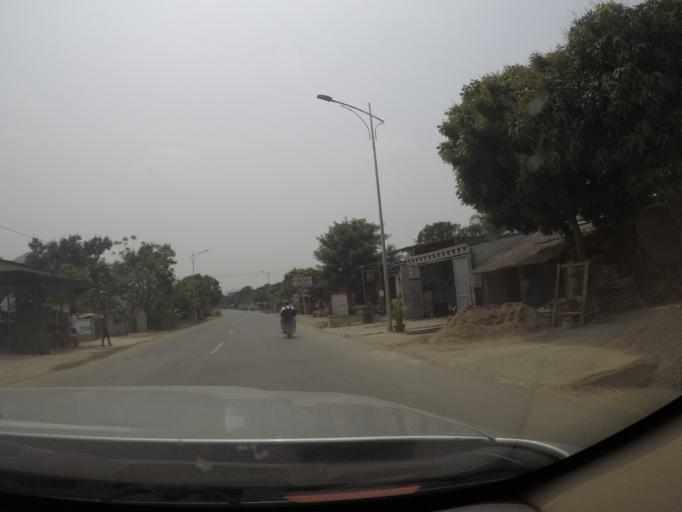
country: VN
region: Thanh Hoa
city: Thi Tran Cam Thuy
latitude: 20.1975
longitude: 105.4769
